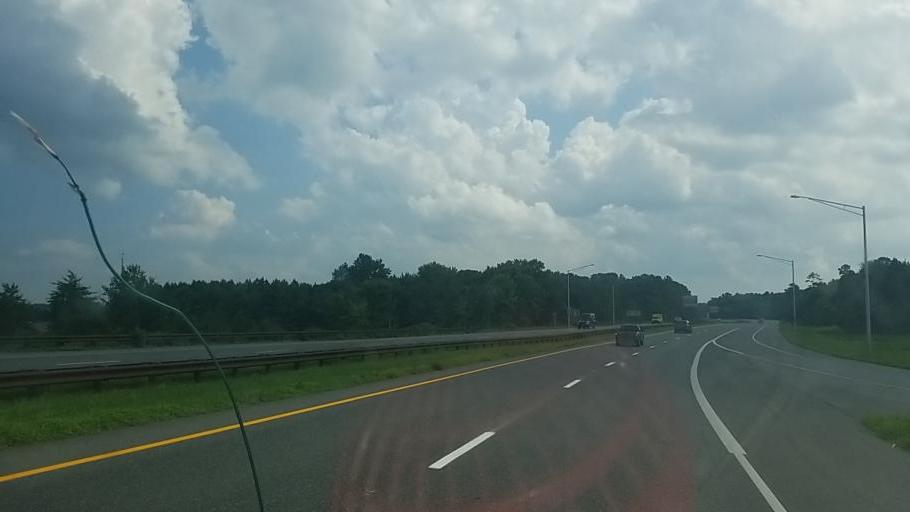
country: US
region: Maryland
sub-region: Worcester County
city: Ocean Pines
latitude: 38.3875
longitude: -75.2035
